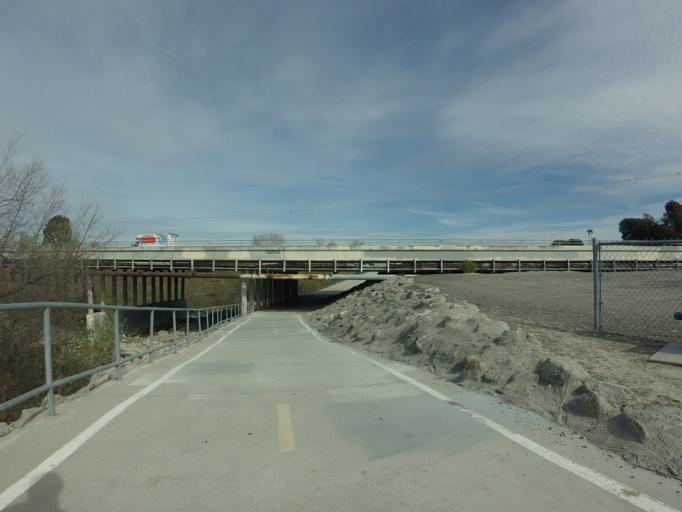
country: US
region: California
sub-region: San Diego County
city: Camp Pendleton South
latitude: 33.2398
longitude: -117.3230
